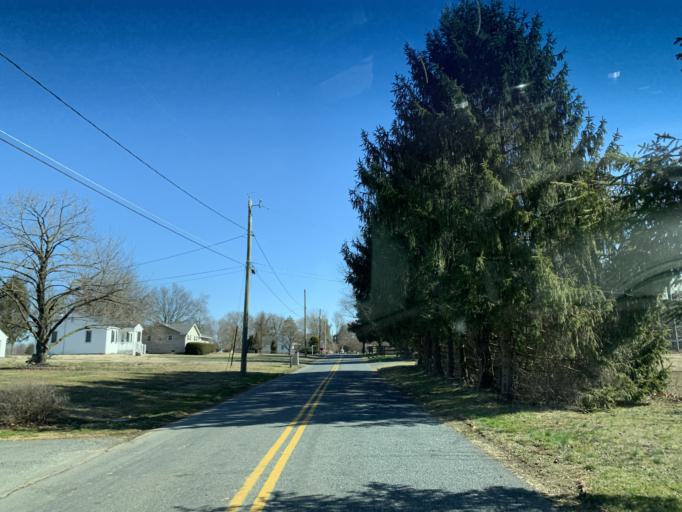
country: US
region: Maryland
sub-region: Harford County
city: Aberdeen
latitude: 39.6354
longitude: -76.2022
